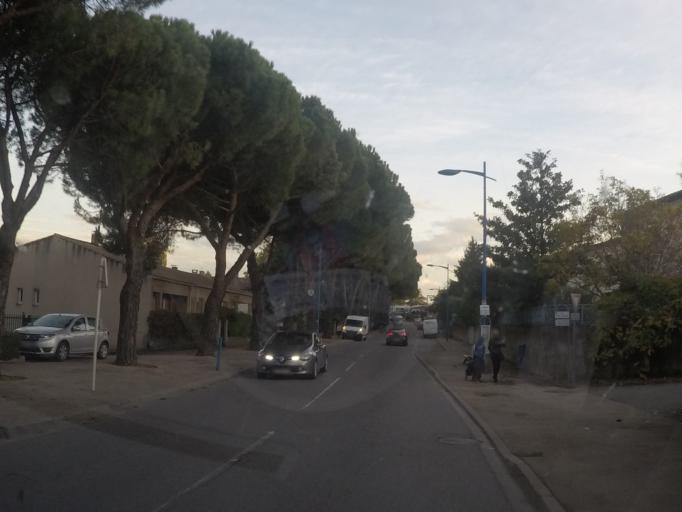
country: FR
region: Provence-Alpes-Cote d'Azur
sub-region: Departement des Alpes-de-Haute-Provence
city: Manosque
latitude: 43.8267
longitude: 5.7819
